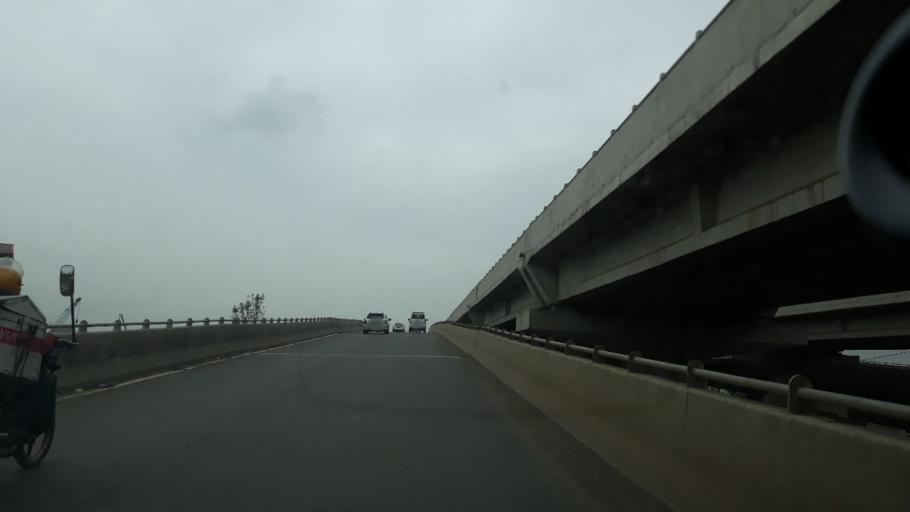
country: KE
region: Nairobi Area
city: Pumwani
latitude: -1.2727
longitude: 36.8816
